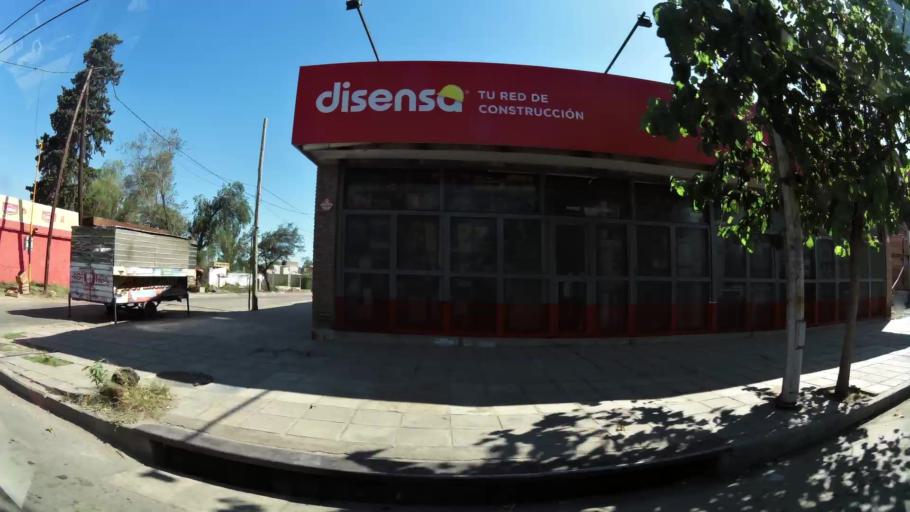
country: AR
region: Cordoba
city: Villa Allende
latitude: -31.3249
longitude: -64.2687
